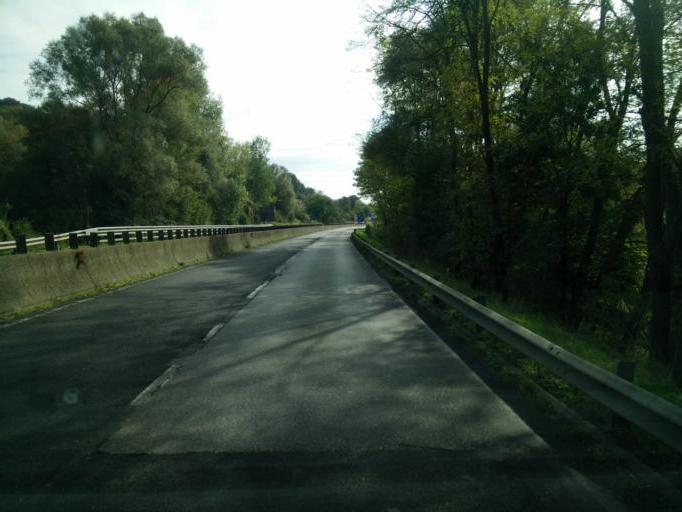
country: IT
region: Tuscany
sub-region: Provincia di Siena
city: Siena
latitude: 43.3139
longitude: 11.3079
